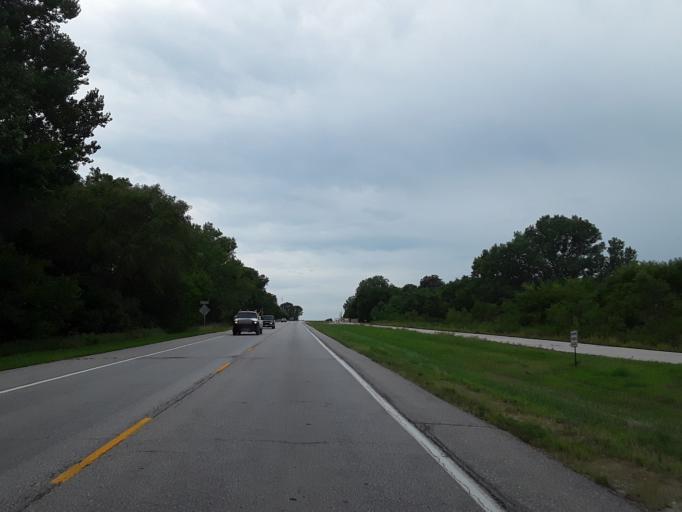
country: US
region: Nebraska
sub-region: Douglas County
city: Bennington
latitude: 41.3651
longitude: -96.0630
